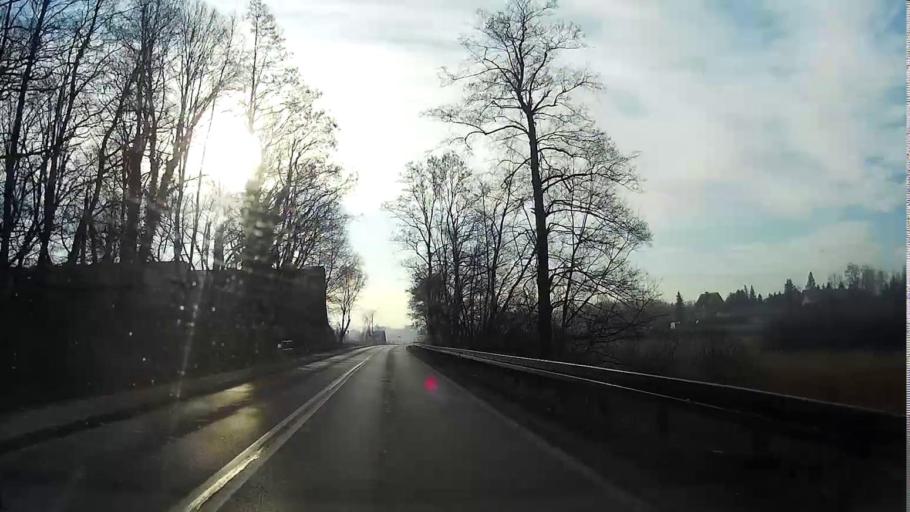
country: PL
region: Lesser Poland Voivodeship
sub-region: Powiat chrzanowski
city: Brodla
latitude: 50.0545
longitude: 19.5664
